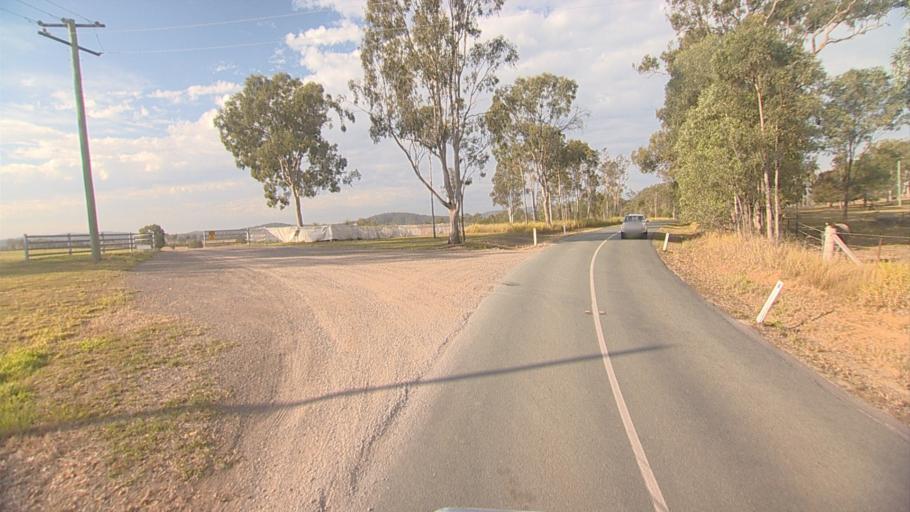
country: AU
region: Queensland
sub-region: Logan
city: Cedar Vale
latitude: -27.8525
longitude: 153.1238
